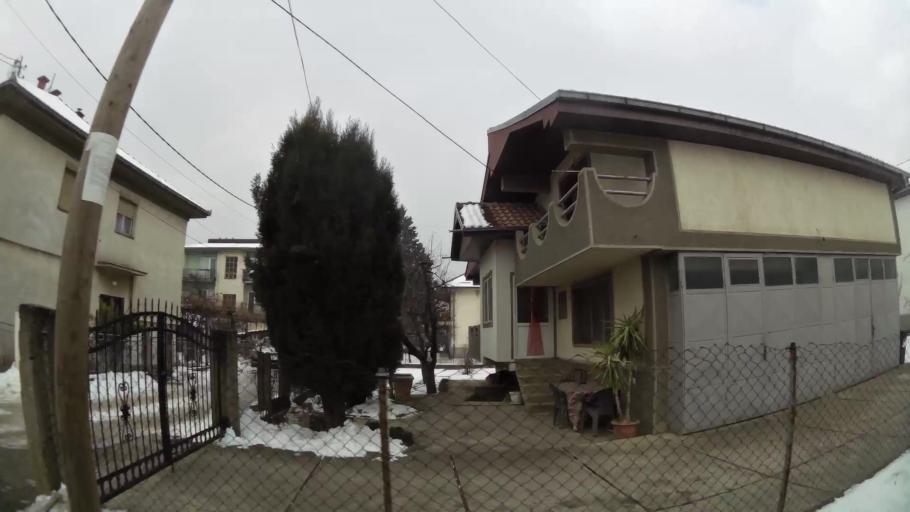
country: MK
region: Saraj
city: Saraj
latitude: 42.0332
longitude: 21.3519
